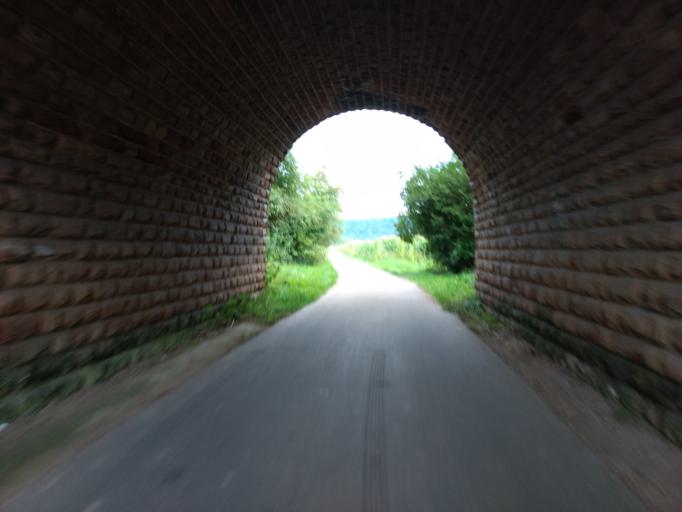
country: DE
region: Saarland
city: Dillingen
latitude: 49.3649
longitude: 6.7073
